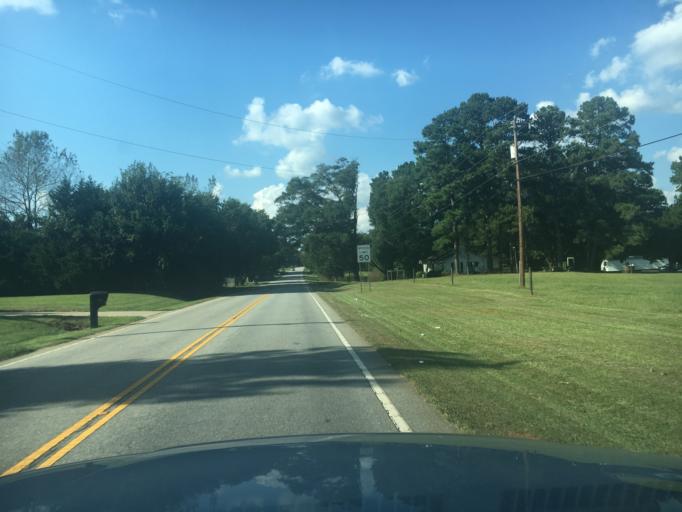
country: US
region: South Carolina
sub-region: Greenville County
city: Fountain Inn
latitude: 34.6103
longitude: -82.2342
